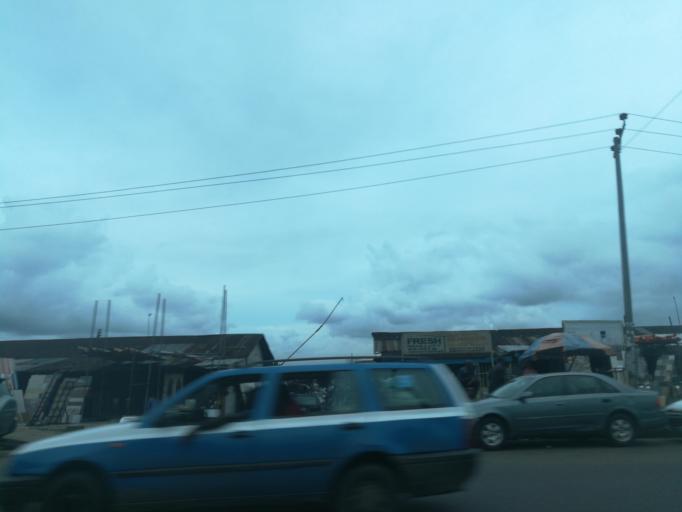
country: NG
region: Rivers
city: Port Harcourt
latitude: 4.8095
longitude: 6.9849
